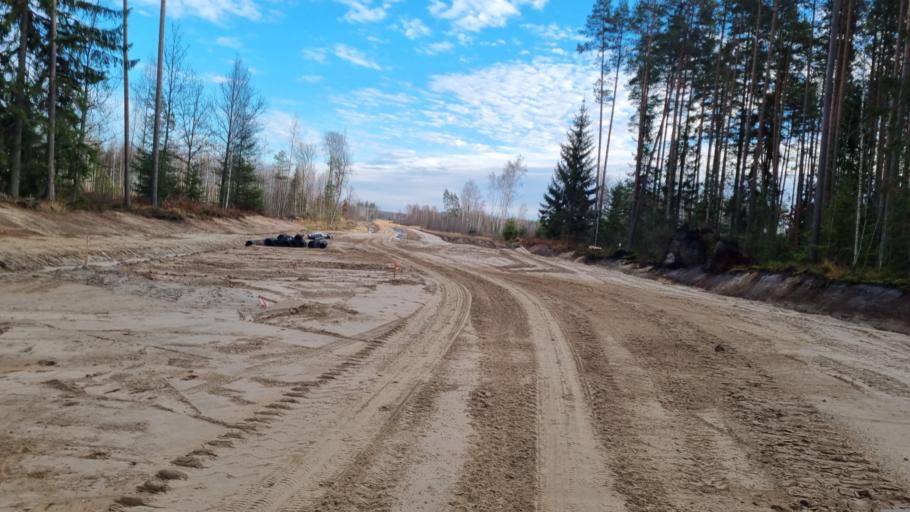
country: LV
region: Kekava
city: Kekava
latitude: 56.7877
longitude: 24.2213
